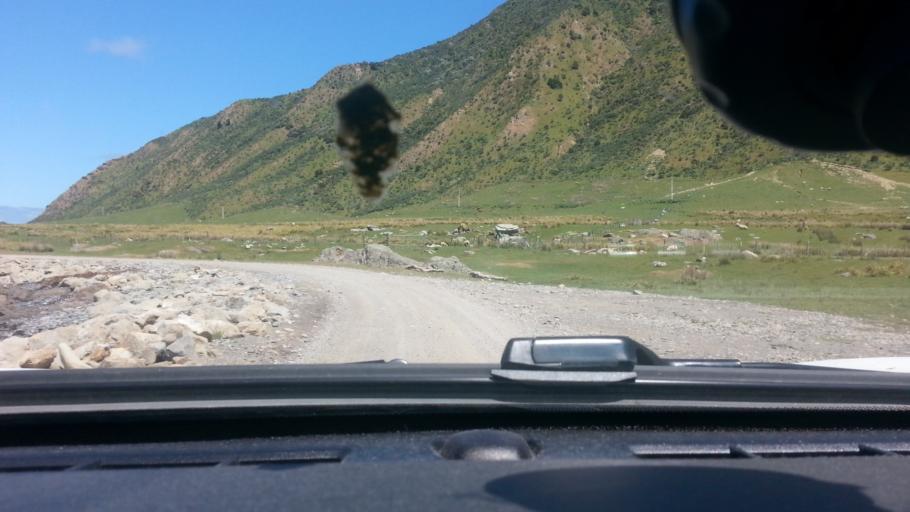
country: NZ
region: Wellington
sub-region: South Wairarapa District
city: Waipawa
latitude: -41.5169
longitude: 175.5042
